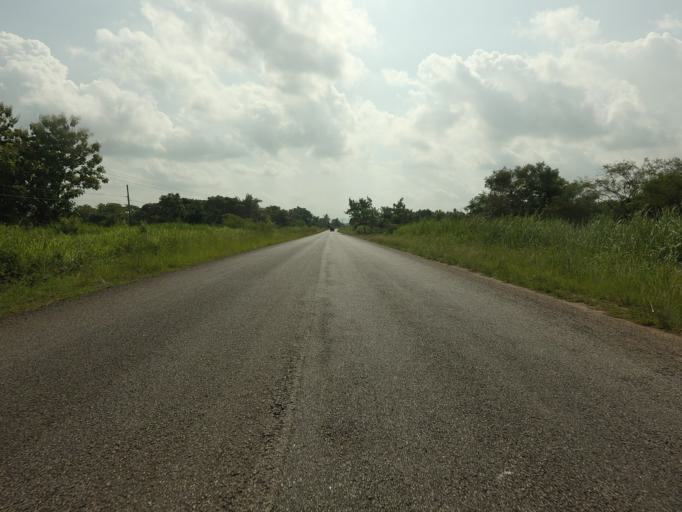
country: GH
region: Volta
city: Ho
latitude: 6.5861
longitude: 0.5708
